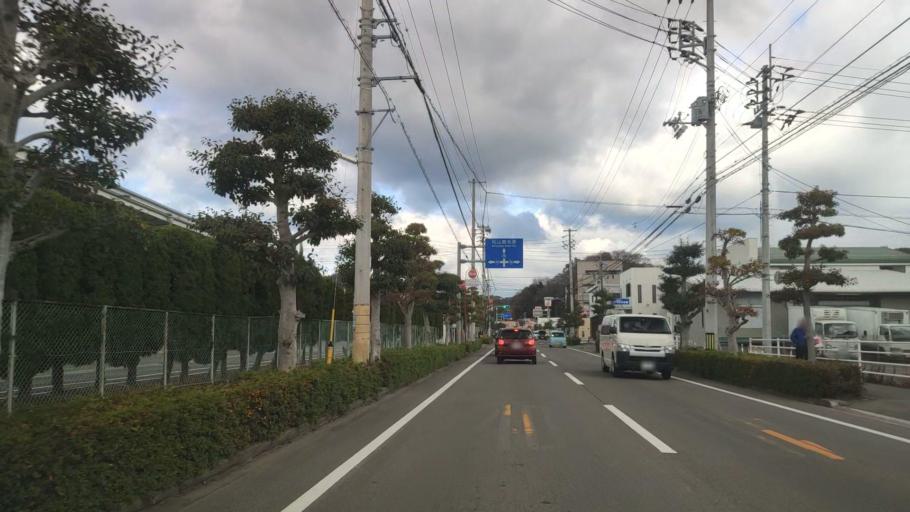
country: JP
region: Ehime
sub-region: Shikoku-chuo Shi
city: Matsuyama
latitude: 33.8656
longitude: 132.7254
